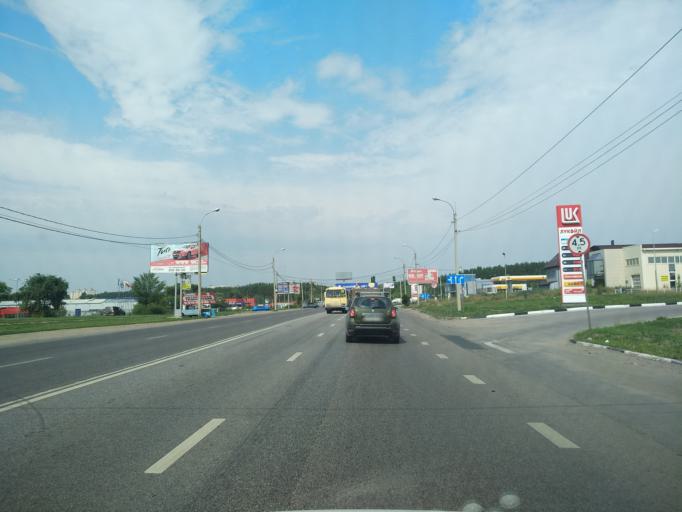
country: RU
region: Voronezj
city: Somovo
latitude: 51.6801
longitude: 39.2869
